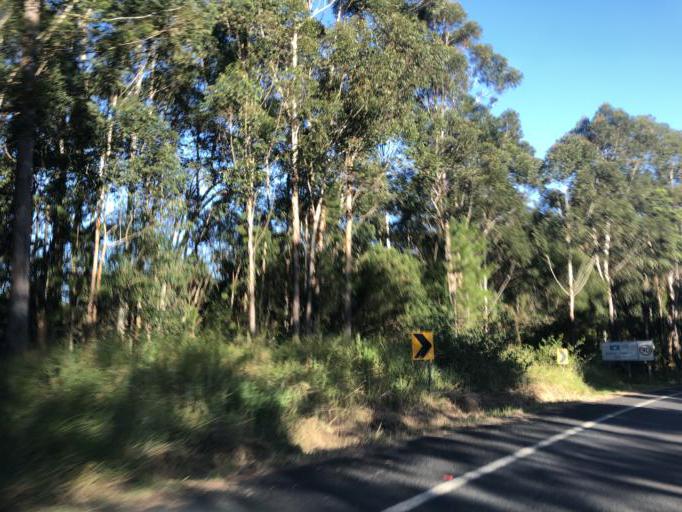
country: AU
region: New South Wales
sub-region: Nambucca Shire
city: Nambucca
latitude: -30.5508
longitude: 153.0086
